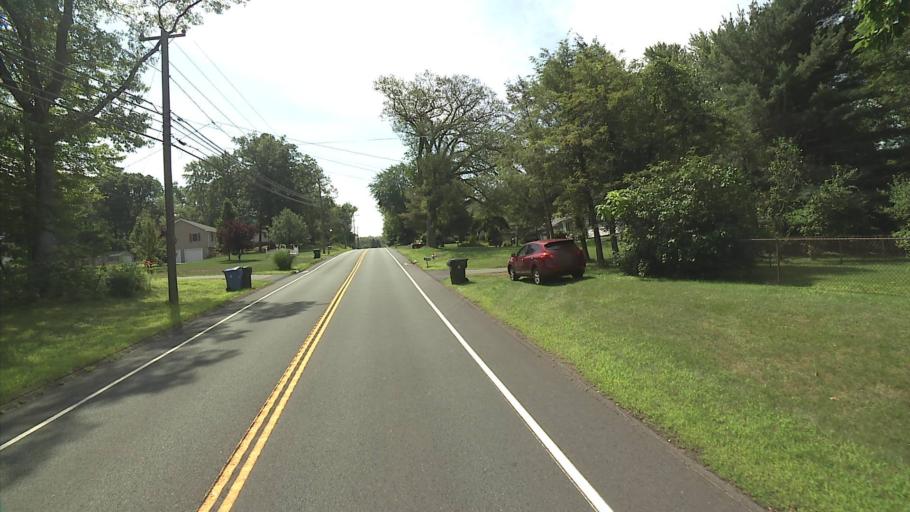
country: US
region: Connecticut
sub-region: Tolland County
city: Rockville
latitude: 41.8495
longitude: -72.4240
